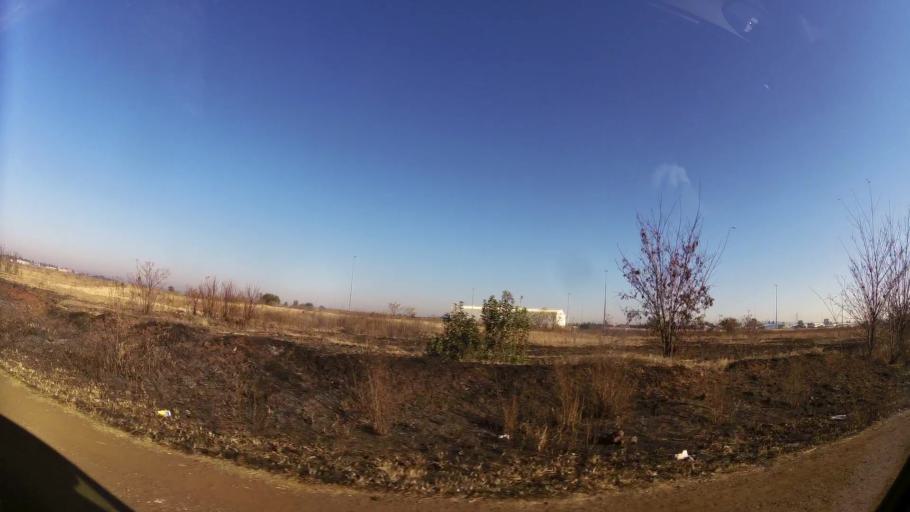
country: ZA
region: Gauteng
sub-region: Ekurhuleni Metropolitan Municipality
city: Germiston
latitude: -26.3325
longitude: 28.1374
